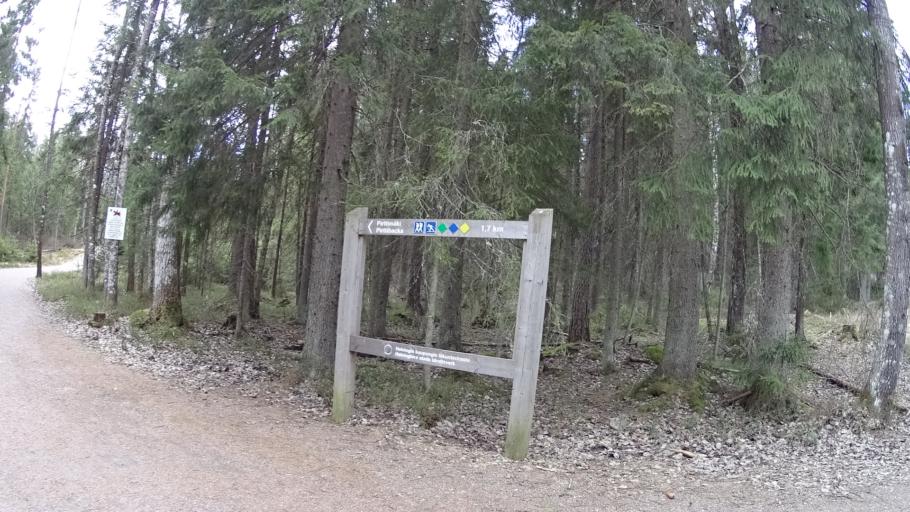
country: FI
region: Uusimaa
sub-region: Helsinki
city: Espoo
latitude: 60.2690
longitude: 24.6326
